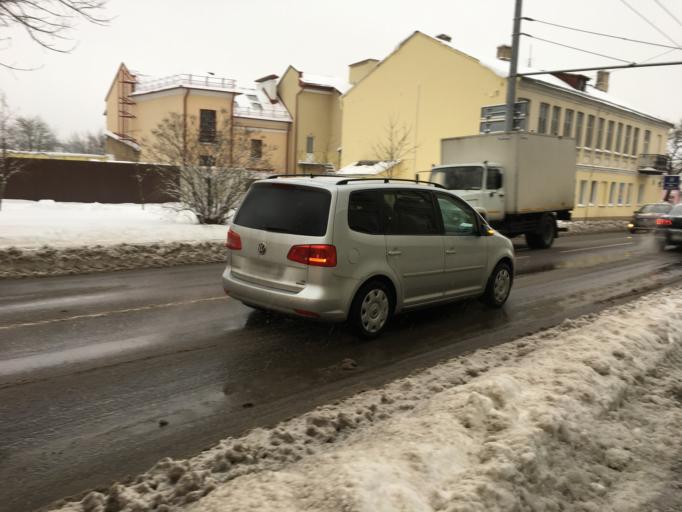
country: BY
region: Grodnenskaya
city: Hrodna
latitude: 53.6808
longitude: 23.8282
